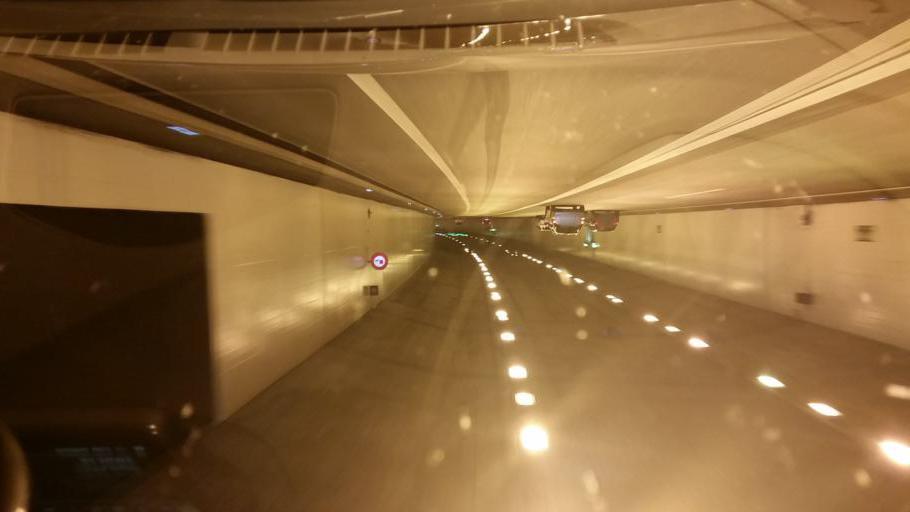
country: CH
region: Lucerne
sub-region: Lucerne-Land District
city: Horw
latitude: 47.0195
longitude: 8.2962
